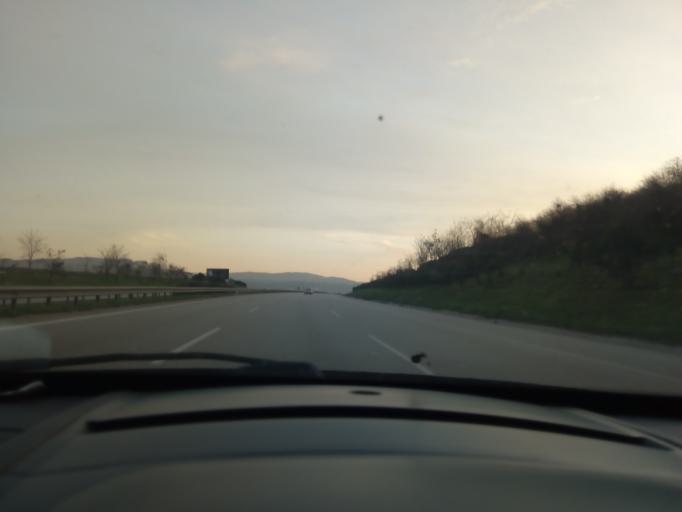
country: TR
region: Bursa
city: Niluefer
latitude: 40.2698
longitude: 28.9591
